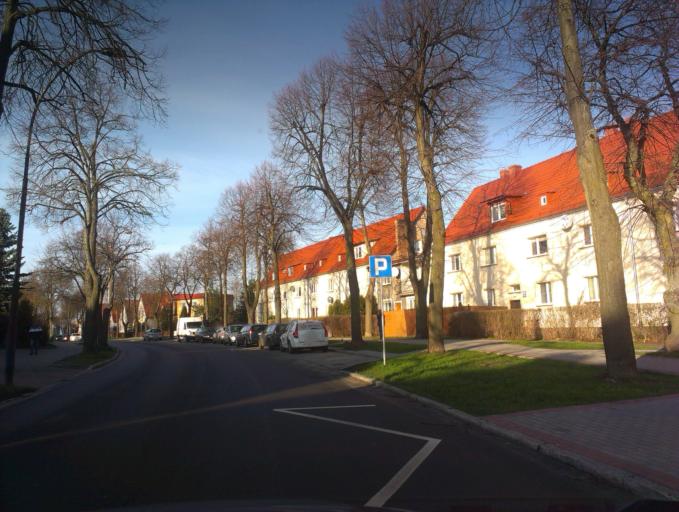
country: PL
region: West Pomeranian Voivodeship
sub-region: Powiat szczecinecki
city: Szczecinek
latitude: 53.7018
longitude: 16.7063
